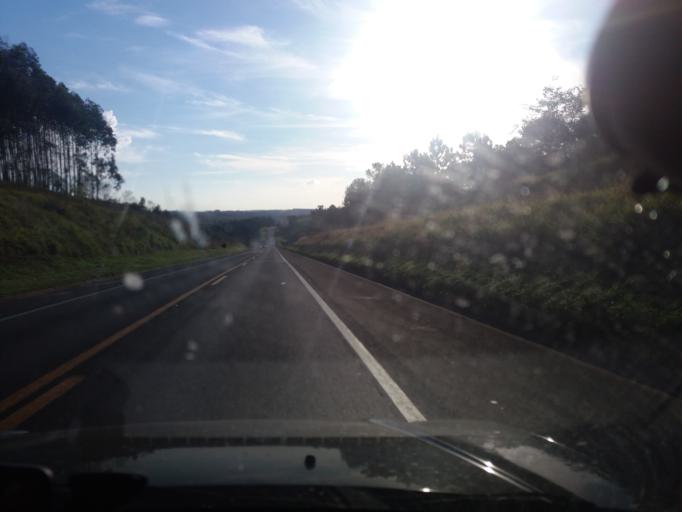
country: BR
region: Sao Paulo
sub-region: Buri
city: Buri
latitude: -23.9365
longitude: -48.6243
